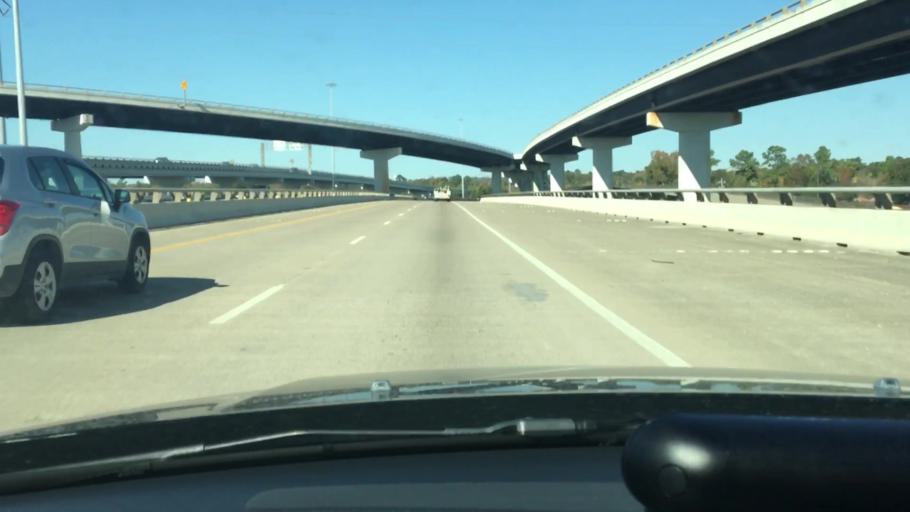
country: US
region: Texas
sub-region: Harris County
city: Cloverleaf
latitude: 29.7731
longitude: -95.1548
